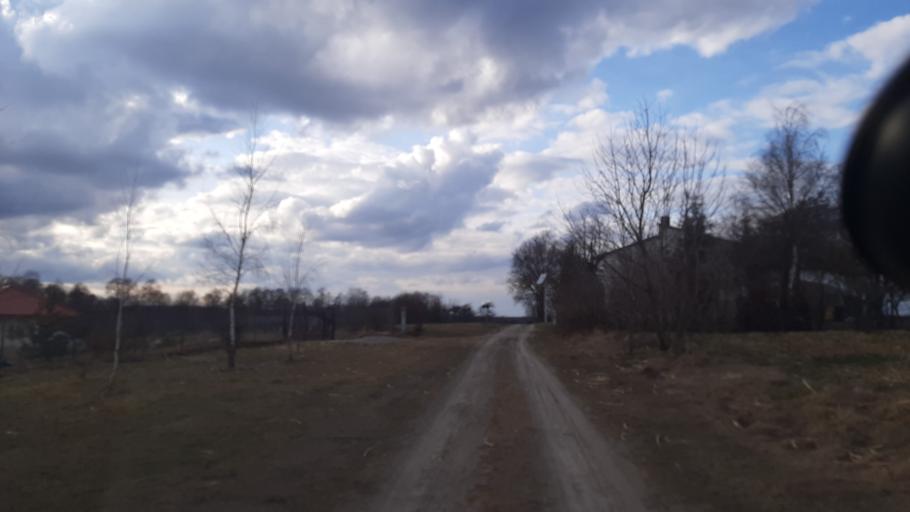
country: PL
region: Lublin Voivodeship
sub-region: Powiat lubelski
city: Jastkow
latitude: 51.3837
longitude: 22.4219
